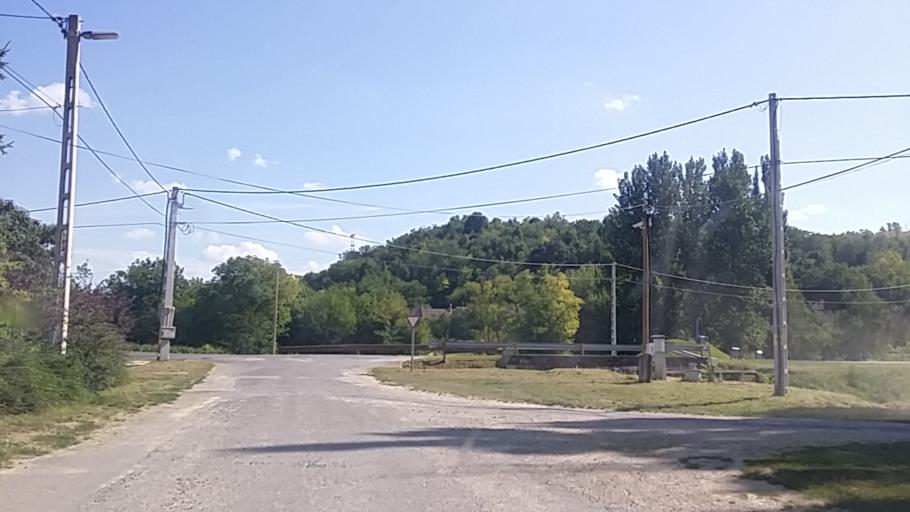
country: HU
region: Tolna
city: Gyonk
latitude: 46.5386
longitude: 18.4736
